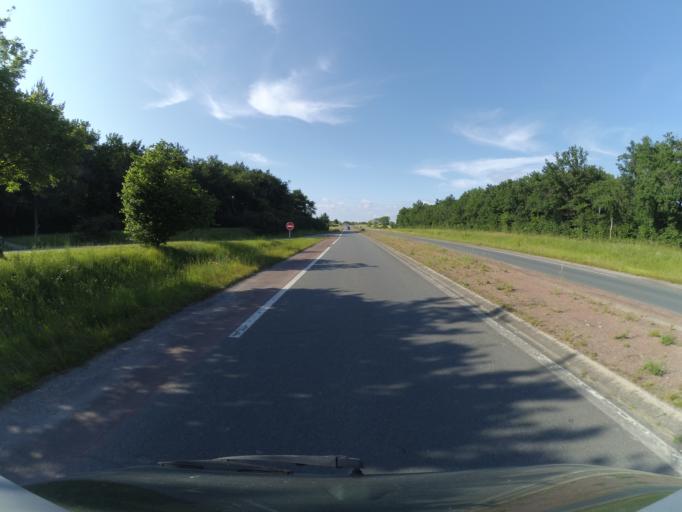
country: FR
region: Poitou-Charentes
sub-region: Departement de la Charente-Maritime
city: Saint-Sulpice-de-Royan
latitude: 45.6769
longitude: -0.9986
